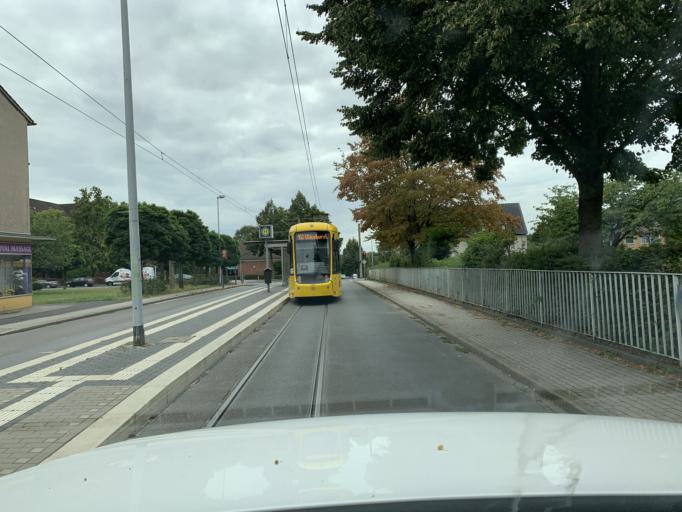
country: DE
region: North Rhine-Westphalia
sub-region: Regierungsbezirk Dusseldorf
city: Oberhausen
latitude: 51.4600
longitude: 6.9002
